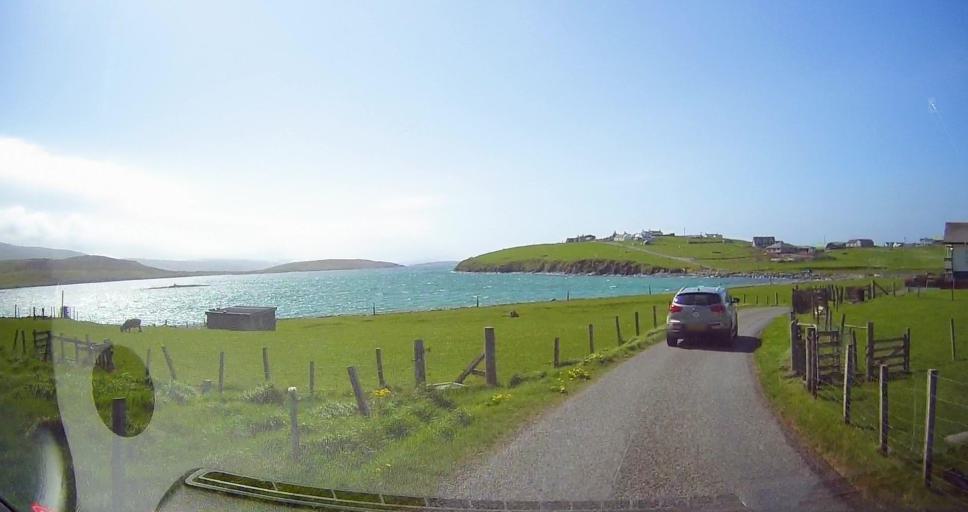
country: GB
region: Scotland
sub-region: Shetland Islands
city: Sandwick
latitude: 60.0655
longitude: -1.3377
